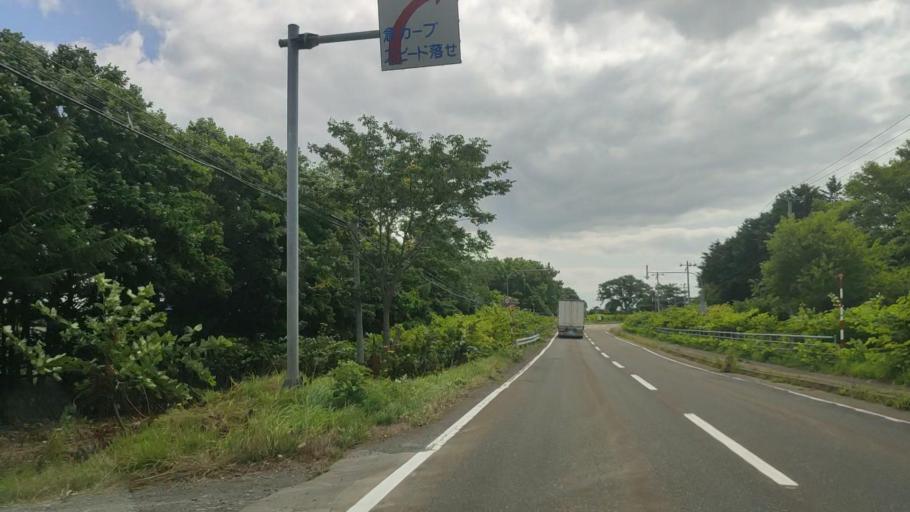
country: JP
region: Hokkaido
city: Rumoi
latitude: 44.5609
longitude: 141.7858
